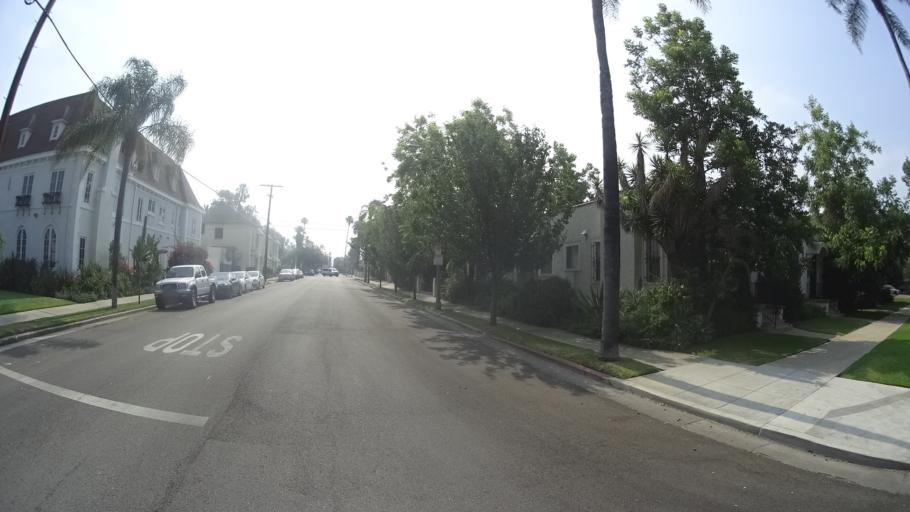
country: US
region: California
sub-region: Los Angeles County
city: View Park-Windsor Hills
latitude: 34.0344
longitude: -118.3211
